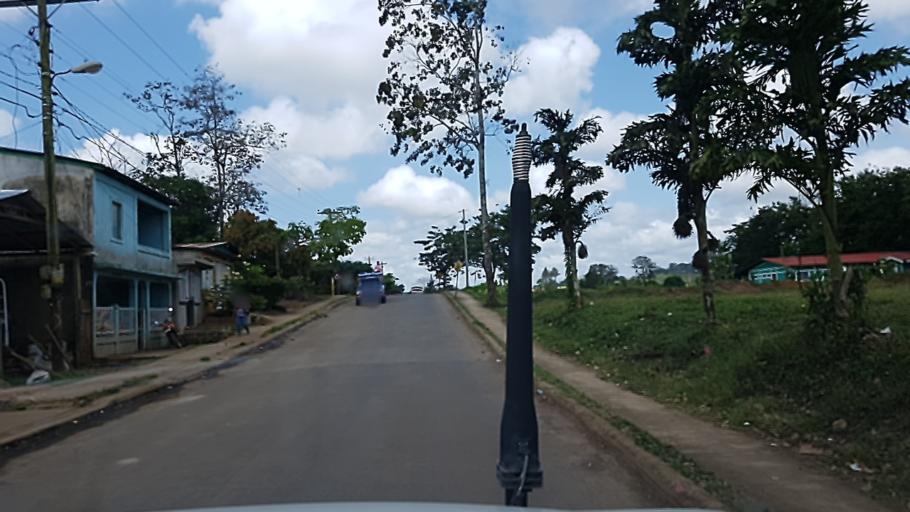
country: NI
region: Atlantico Sur
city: Nueva Guinea
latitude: 11.6867
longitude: -84.4564
